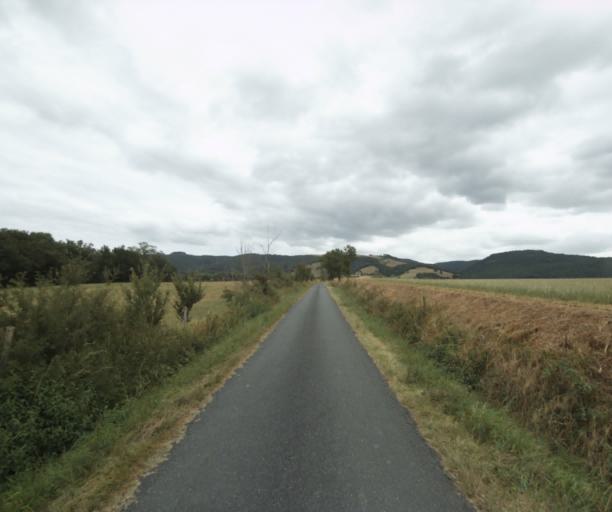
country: FR
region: Midi-Pyrenees
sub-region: Departement du Tarn
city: Soreze
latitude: 43.4656
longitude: 2.0686
